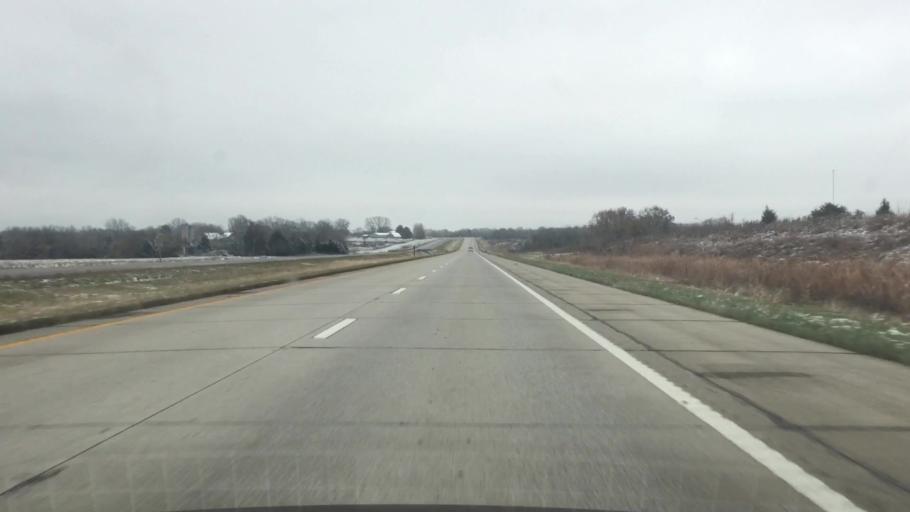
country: US
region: Missouri
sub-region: Saint Clair County
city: Osceola
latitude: 38.1980
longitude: -93.7466
